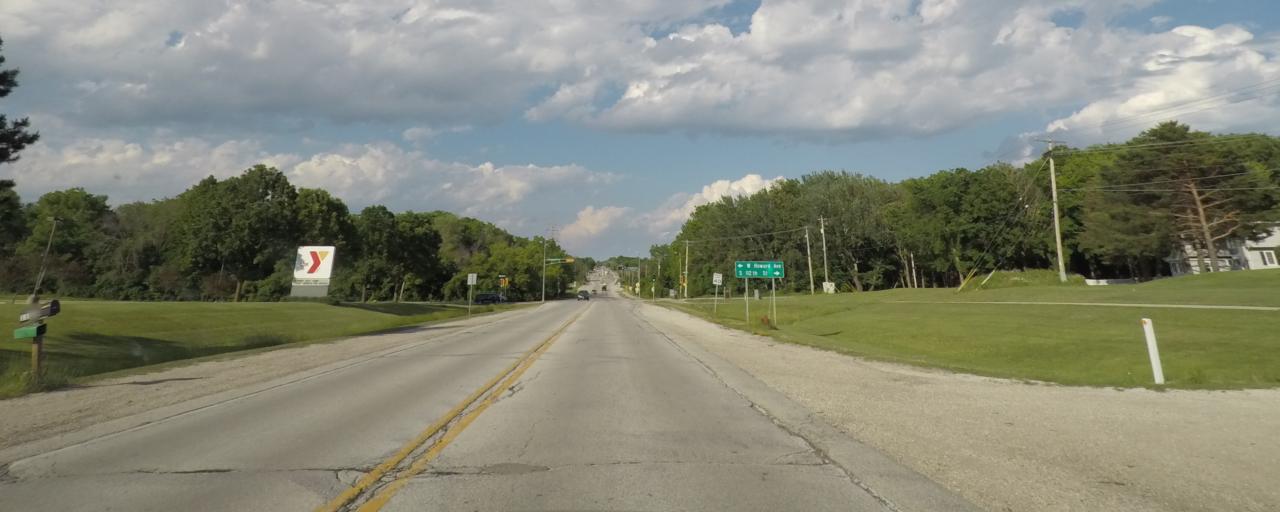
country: US
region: Wisconsin
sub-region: Milwaukee County
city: Hales Corners
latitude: 42.9715
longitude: -88.0550
